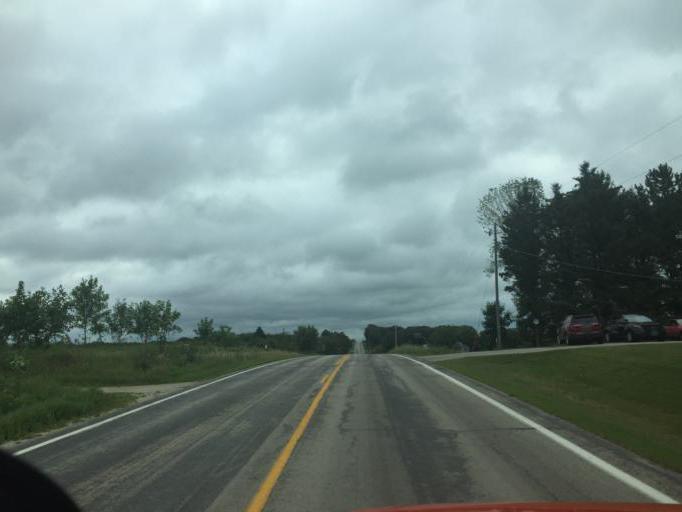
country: US
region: Minnesota
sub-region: Olmsted County
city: Rochester
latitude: 43.9640
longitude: -92.5328
